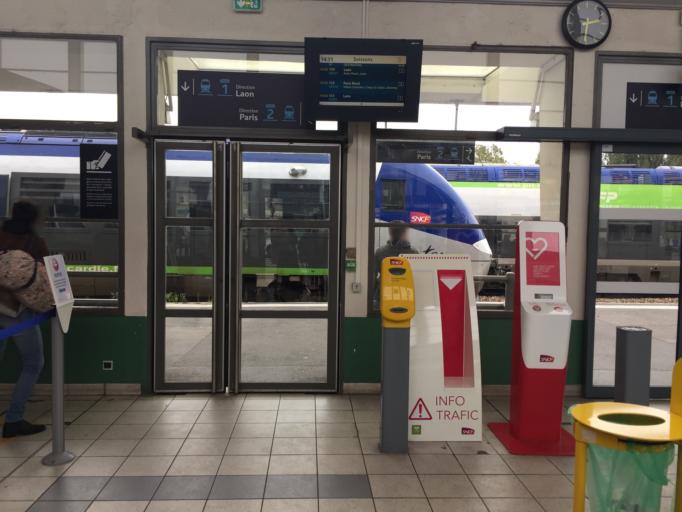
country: FR
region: Picardie
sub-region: Departement de l'Aisne
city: Belleu
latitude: 49.3692
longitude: 3.3382
